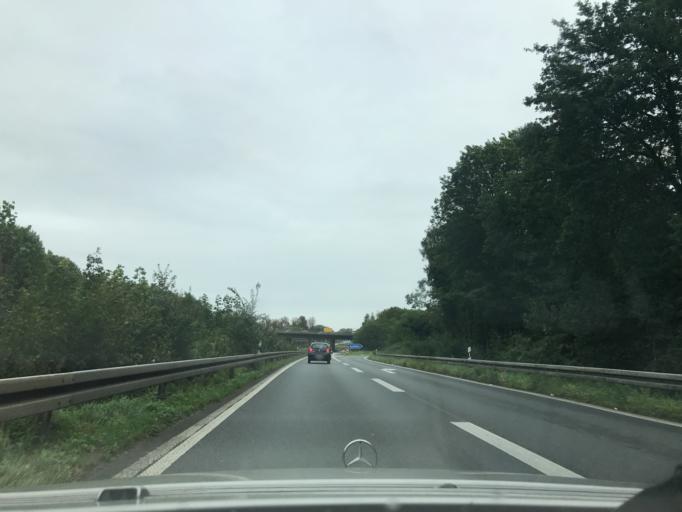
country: DE
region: North Rhine-Westphalia
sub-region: Regierungsbezirk Dusseldorf
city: Ratingen
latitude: 51.2938
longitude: 6.8854
